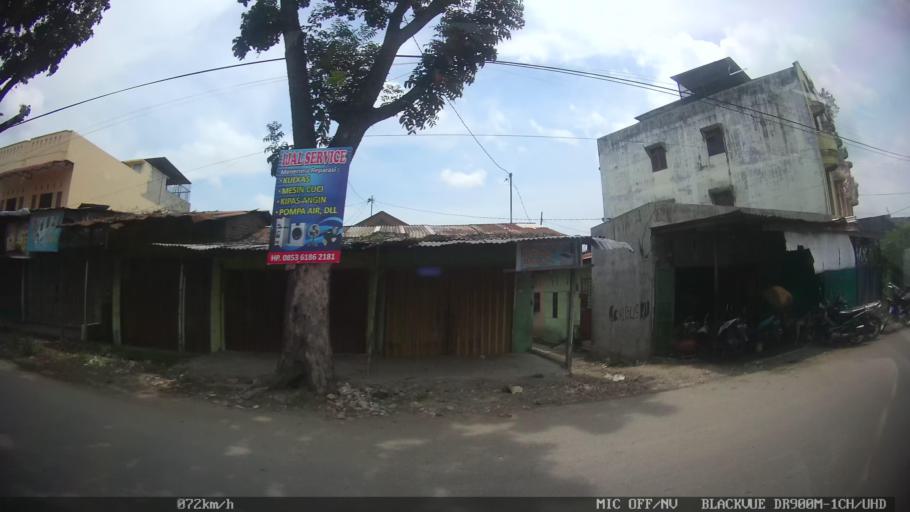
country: ID
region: North Sumatra
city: Labuhan Deli
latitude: 3.6984
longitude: 98.6748
